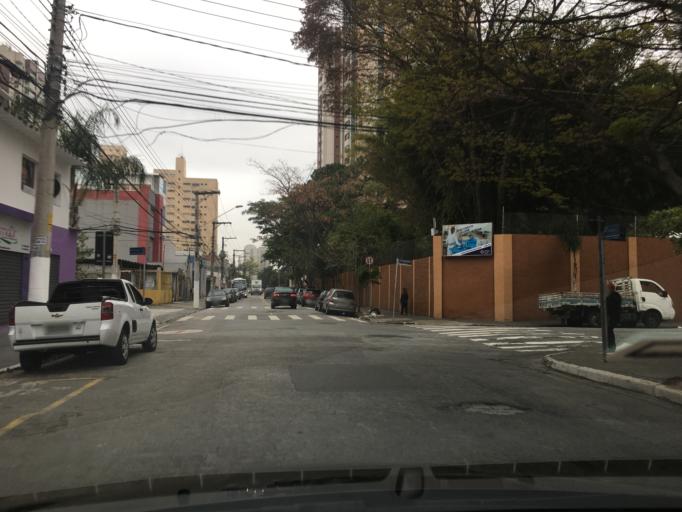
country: BR
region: Sao Paulo
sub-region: Sao Paulo
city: Sao Paulo
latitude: -23.5387
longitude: -46.5770
